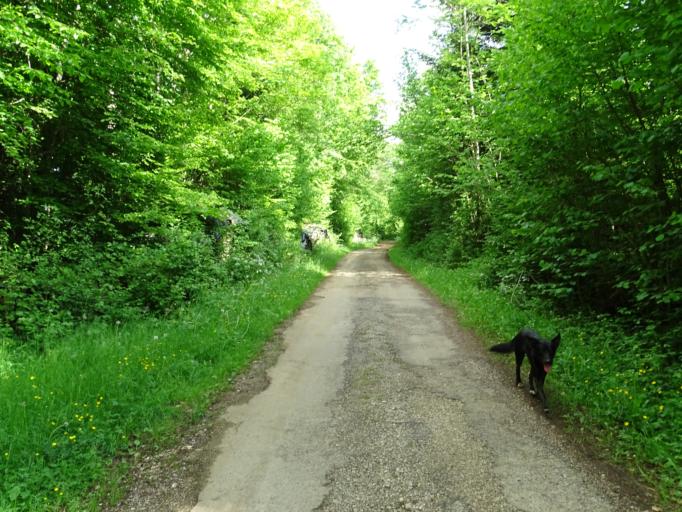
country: FR
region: Franche-Comte
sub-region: Departement du Doubs
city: Levier
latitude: 47.0105
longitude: 6.0112
